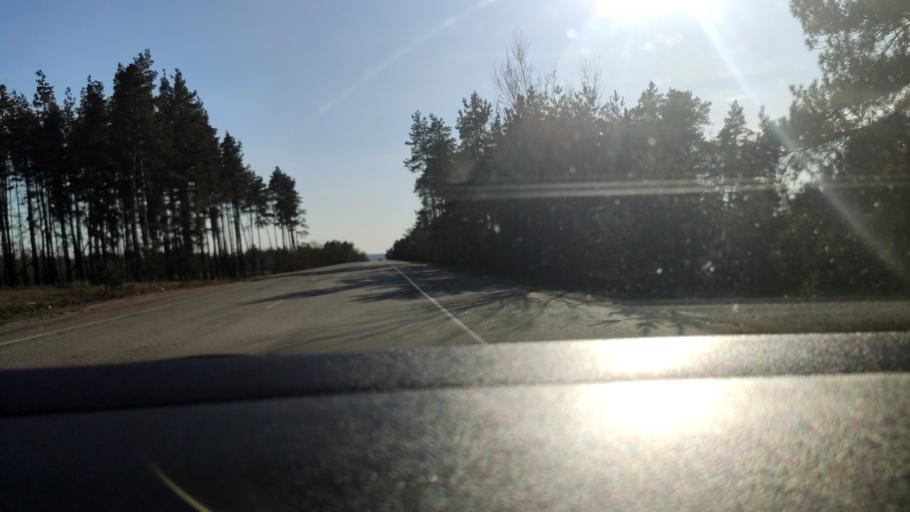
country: RU
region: Voronezj
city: Kolodeznyy
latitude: 51.3664
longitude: 39.1968
